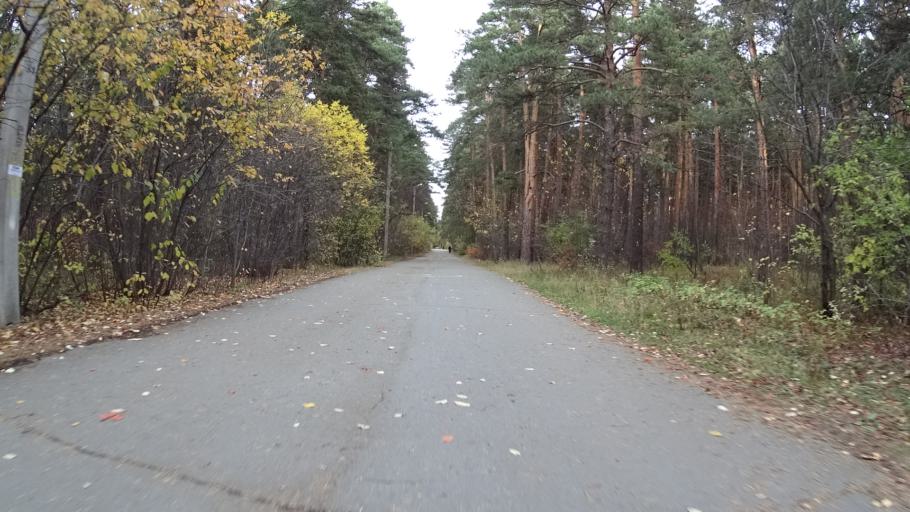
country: RU
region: Chelyabinsk
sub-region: Gorod Chelyabinsk
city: Chelyabinsk
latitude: 55.1522
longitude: 61.3581
